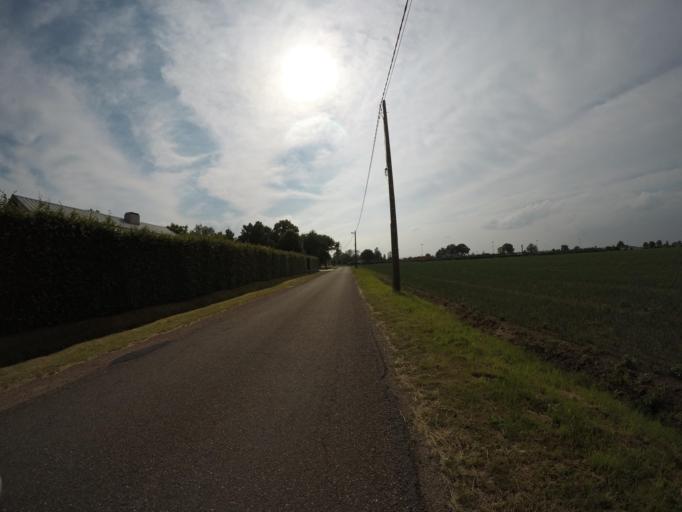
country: BE
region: Flanders
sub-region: Provincie Antwerpen
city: Rijkevorsel
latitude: 51.3594
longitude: 4.7282
